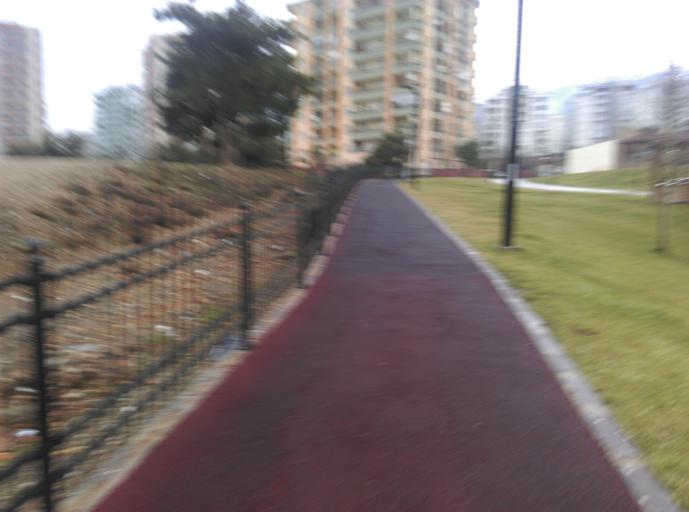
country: TR
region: Kahramanmaras
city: Kahramanmaras
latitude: 37.5815
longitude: 36.8893
